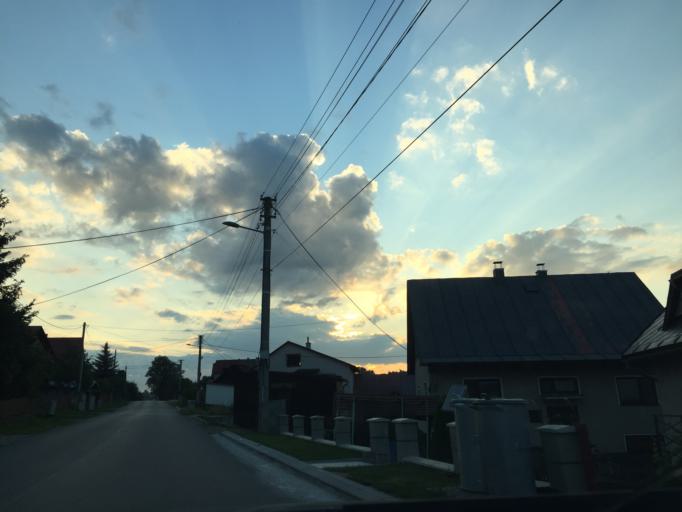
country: PL
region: Silesian Voivodeship
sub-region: Powiat zywiecki
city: Korbielow
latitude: 49.4615
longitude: 19.3508
